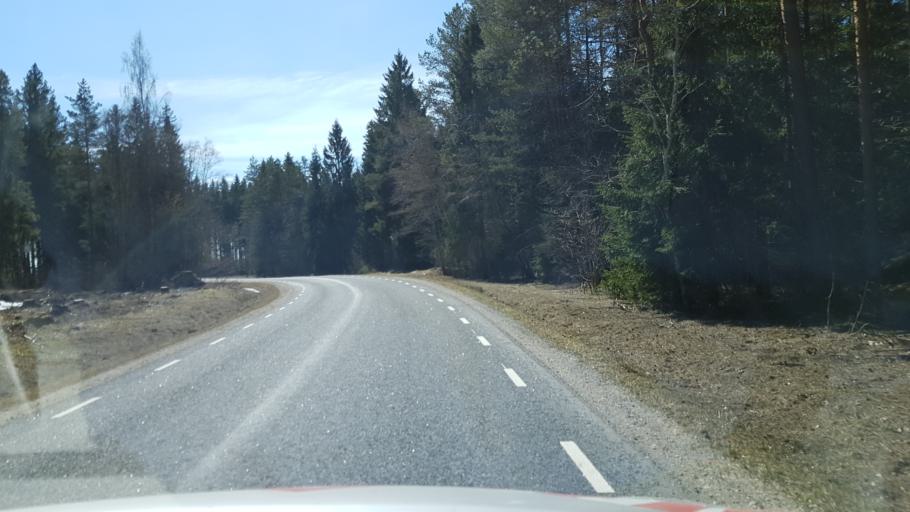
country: EE
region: Laeaene-Virumaa
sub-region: Vinni vald
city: Vinni
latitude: 59.1275
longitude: 26.5212
